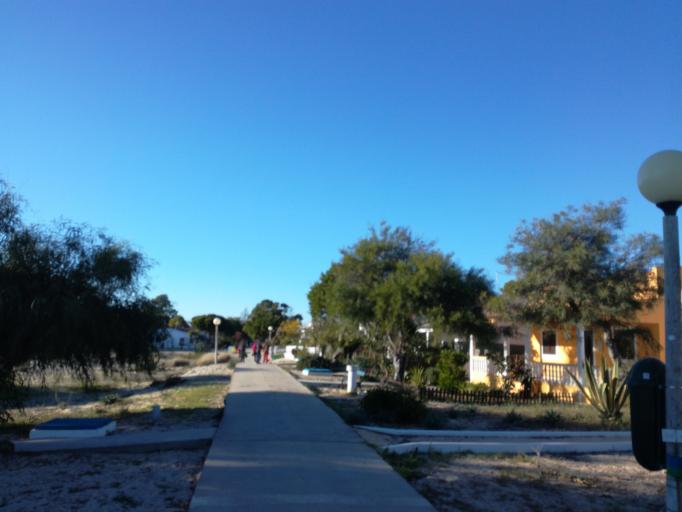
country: PT
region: Faro
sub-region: Olhao
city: Olhao
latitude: 37.0174
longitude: -7.7989
